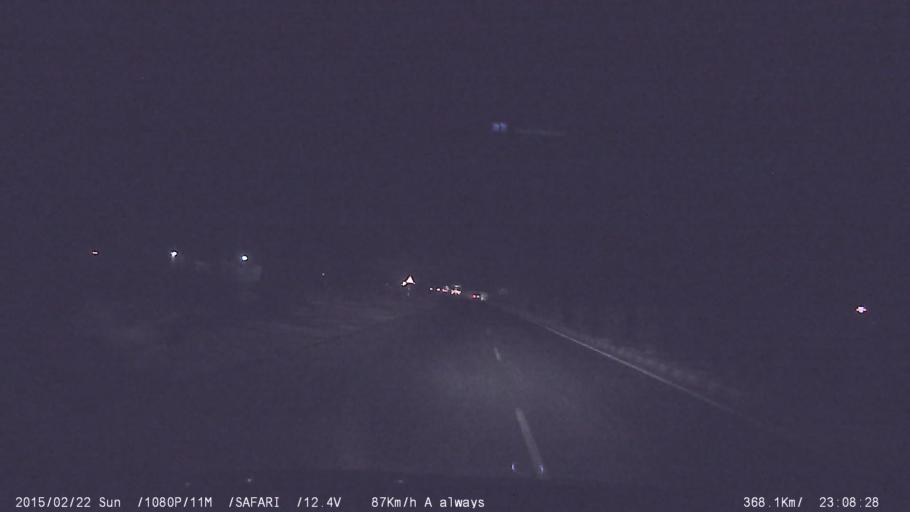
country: IN
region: Tamil Nadu
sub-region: Namakkal
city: Rasipuram
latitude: 11.4532
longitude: 78.1588
